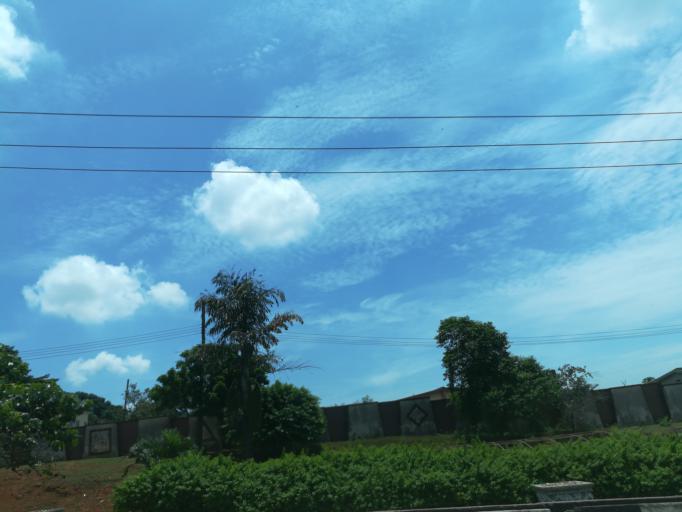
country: NG
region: Lagos
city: Ebute Ikorodu
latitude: 6.6064
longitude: 3.4965
